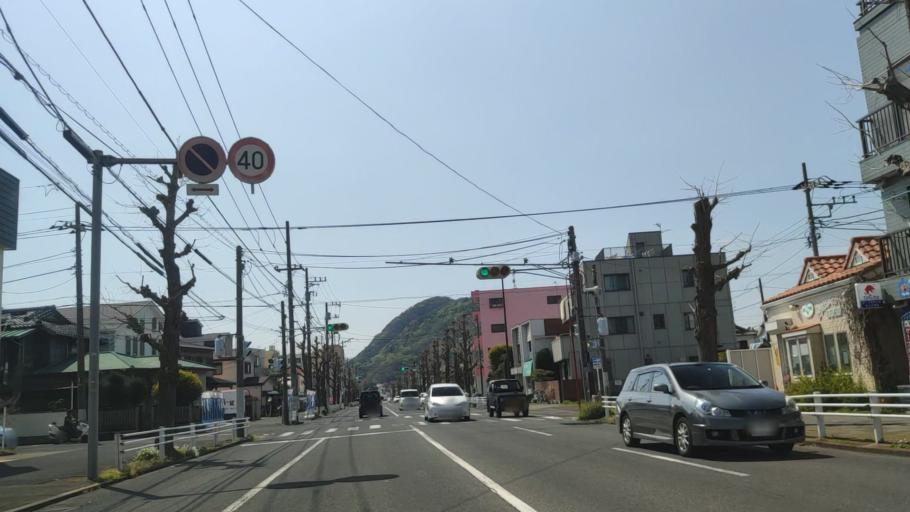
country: JP
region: Kanagawa
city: Hiratsuka
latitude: 35.3268
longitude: 139.3359
